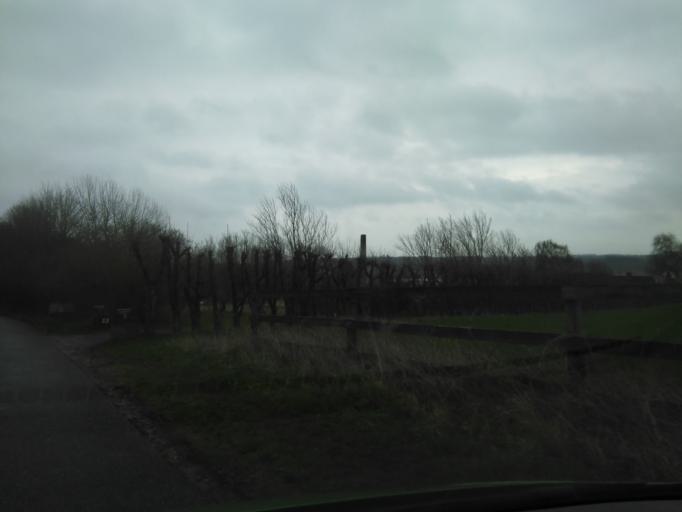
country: DK
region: Central Jutland
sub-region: Arhus Kommune
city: Kolt
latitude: 56.1513
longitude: 10.0756
